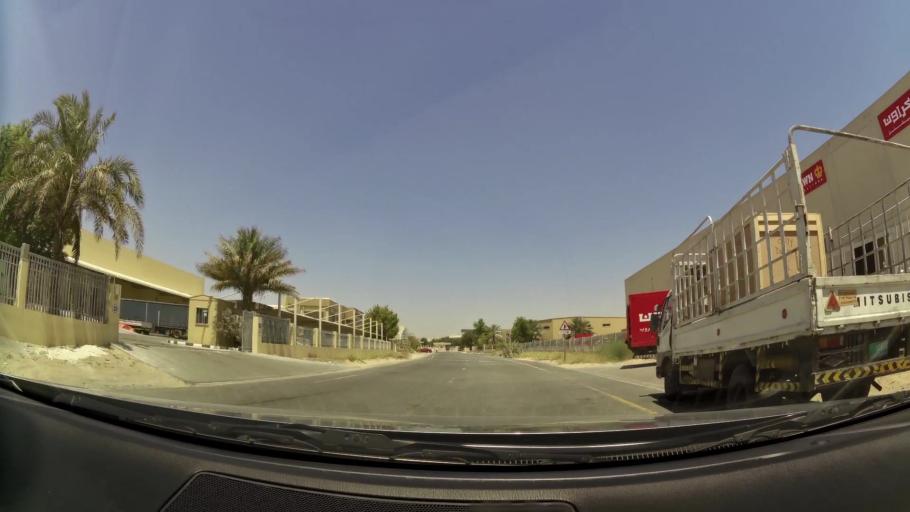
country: AE
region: Dubai
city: Dubai
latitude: 24.9831
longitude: 55.1897
